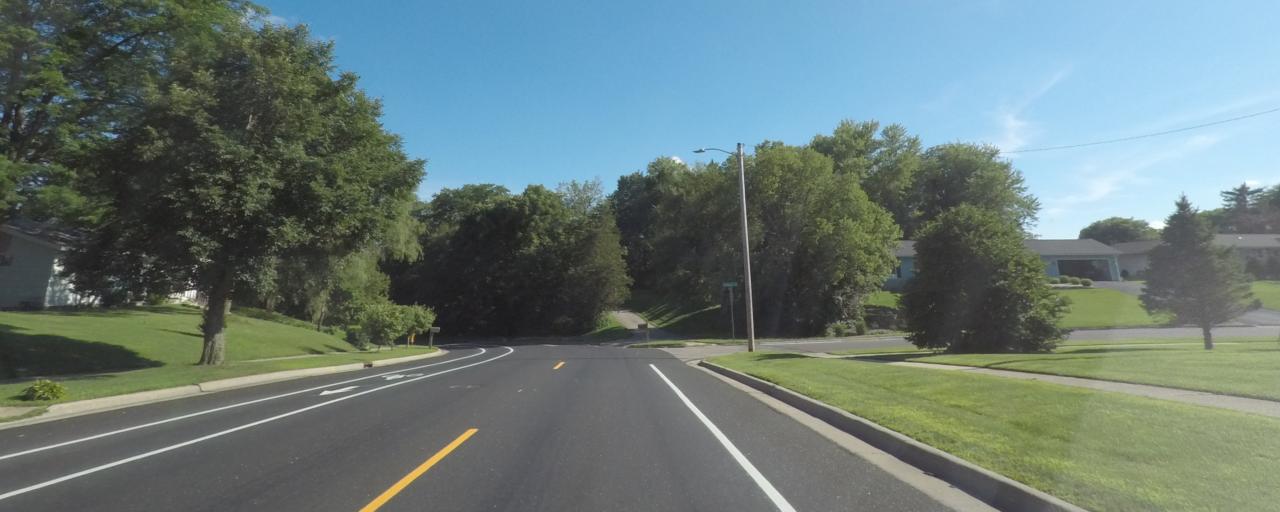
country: US
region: Wisconsin
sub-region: Rock County
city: Janesville
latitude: 42.6879
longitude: -88.9877
